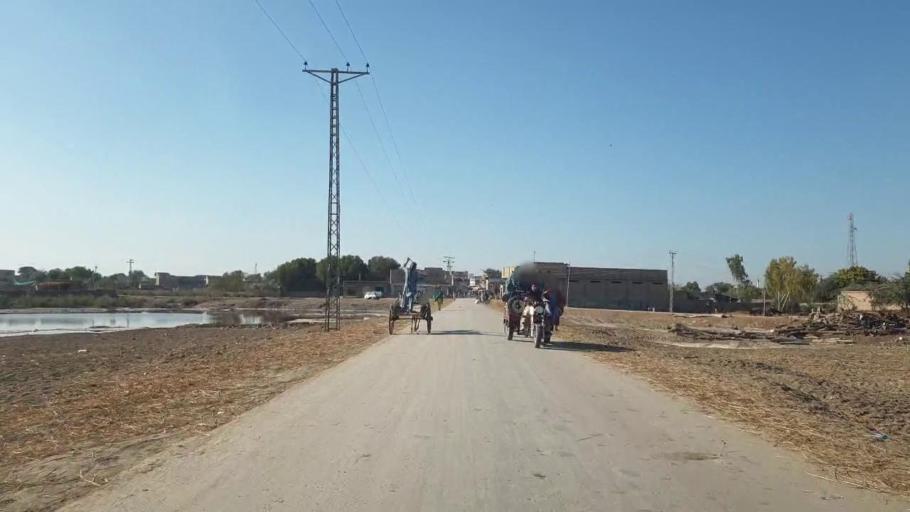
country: PK
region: Sindh
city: New Badah
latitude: 27.3265
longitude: 68.0298
